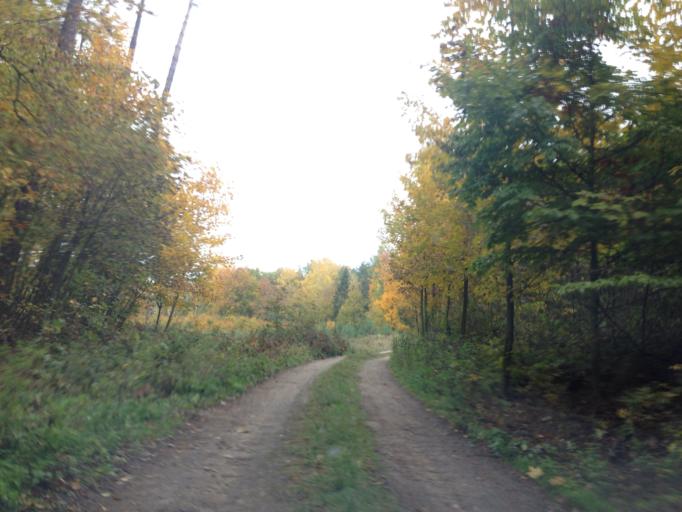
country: PL
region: Kujawsko-Pomorskie
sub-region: Powiat brodnicki
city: Gorzno
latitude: 53.2573
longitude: 19.6901
